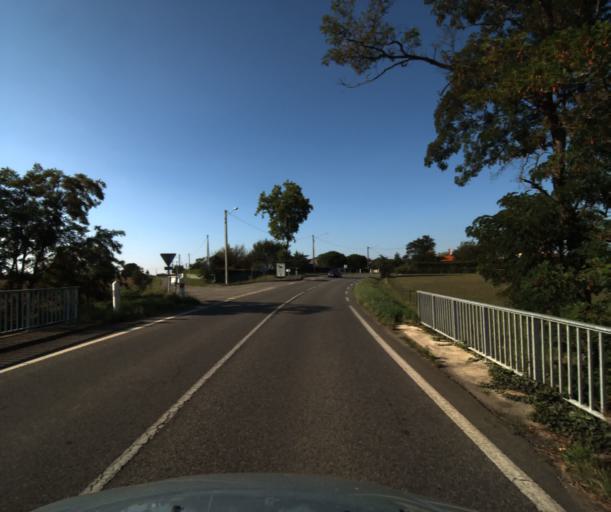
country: FR
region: Midi-Pyrenees
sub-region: Departement de la Haute-Garonne
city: Labarthe-sur-Leze
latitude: 43.4367
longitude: 1.3786
